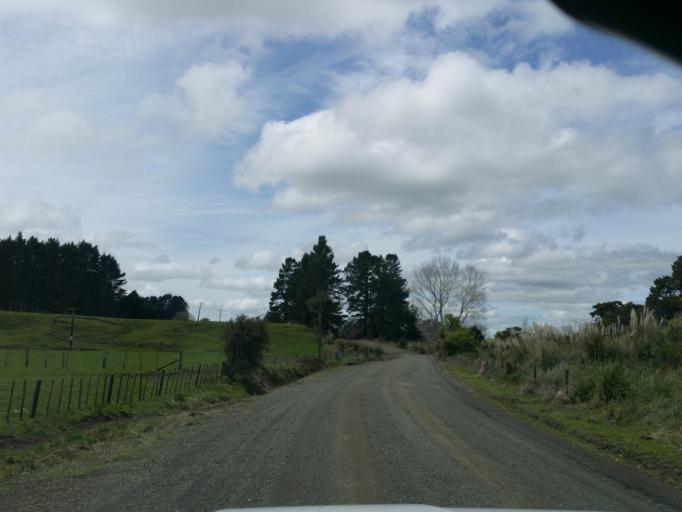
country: NZ
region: Northland
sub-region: Whangarei
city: Maungatapere
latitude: -35.8960
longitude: 174.0836
